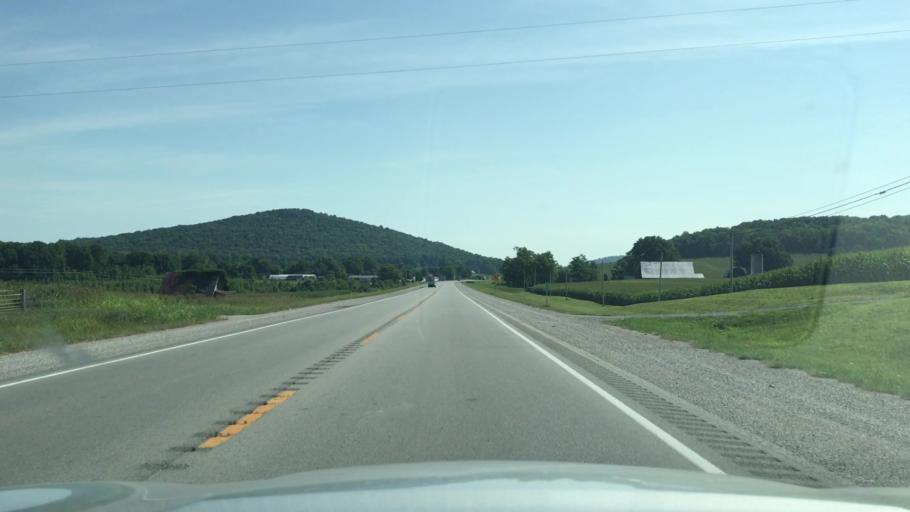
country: US
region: Kentucky
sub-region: Wayne County
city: Monticello
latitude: 36.7842
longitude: -84.9483
